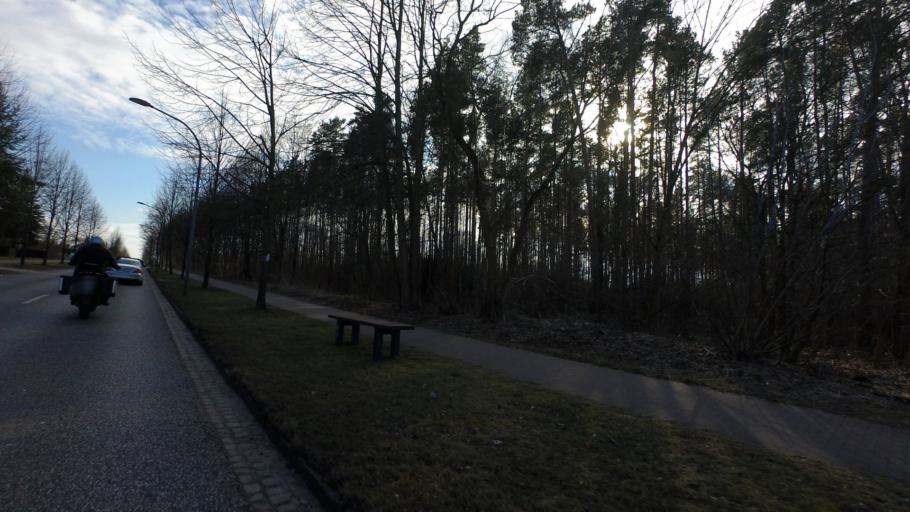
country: DE
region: Brandenburg
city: Birkenwerder
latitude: 52.6806
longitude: 13.2814
